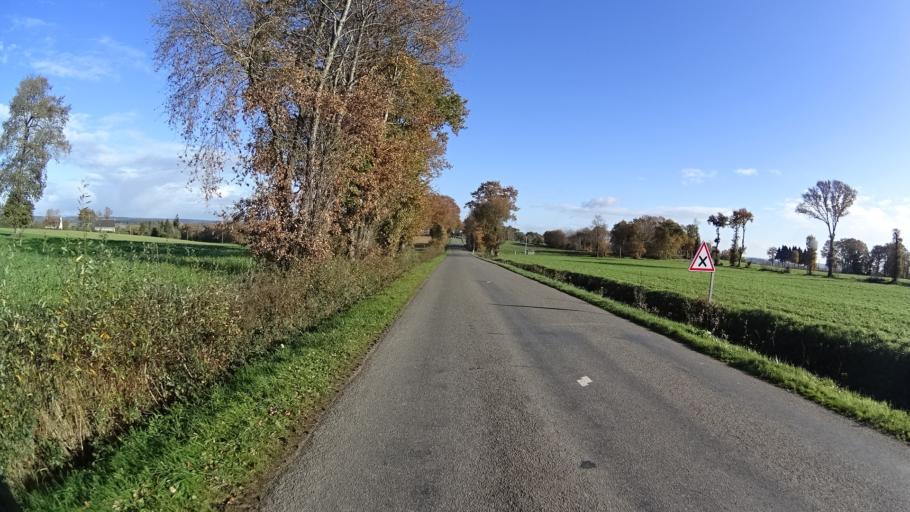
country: FR
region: Brittany
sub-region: Departement du Morbihan
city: Saint-Martin-sur-Oust
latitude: 47.7944
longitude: -2.2021
